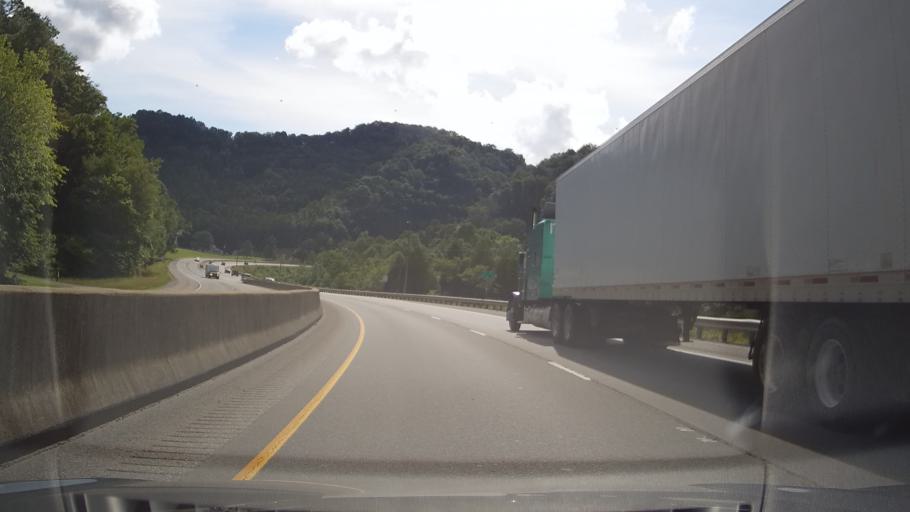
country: US
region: Kentucky
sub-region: Floyd County
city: Prestonsburg
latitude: 37.6233
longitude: -82.7283
